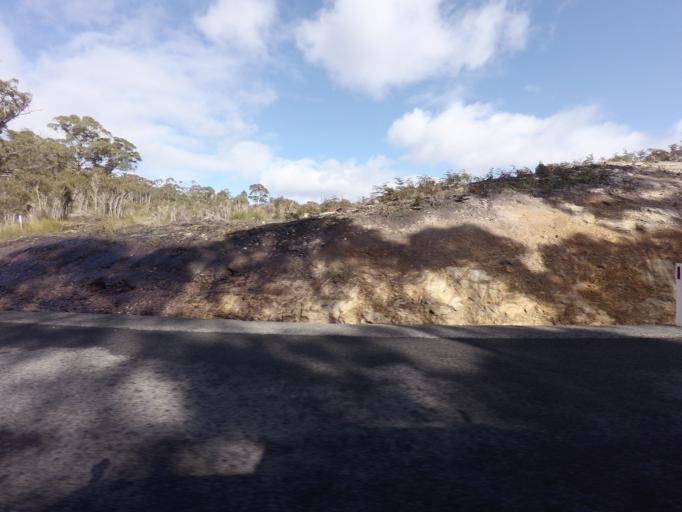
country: AU
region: Tasmania
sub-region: Huon Valley
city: Geeveston
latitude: -43.4261
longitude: 146.9055
